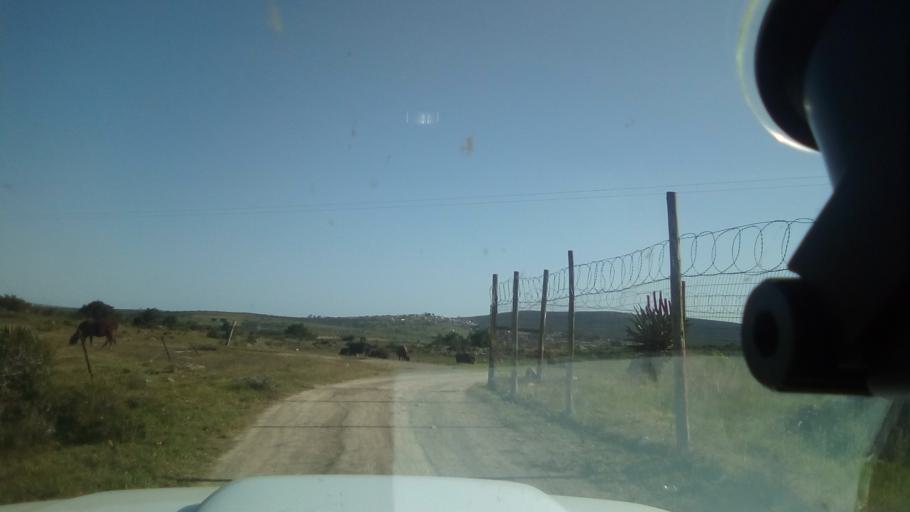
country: ZA
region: Eastern Cape
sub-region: Buffalo City Metropolitan Municipality
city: Bhisho
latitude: -32.8224
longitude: 27.3547
